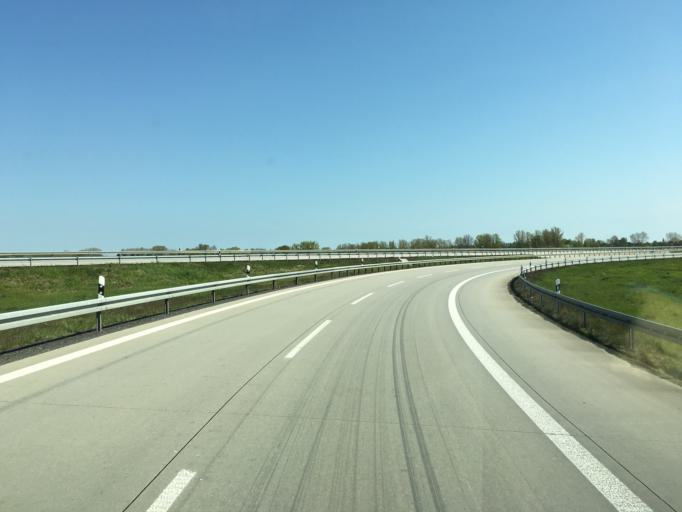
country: DE
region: Saxony
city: Borsdorf
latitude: 51.3134
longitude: 12.5483
